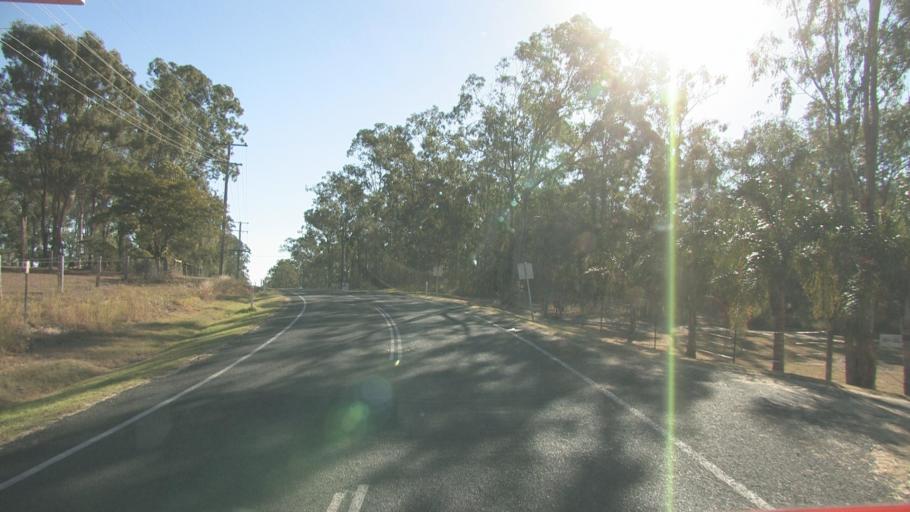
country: AU
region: Queensland
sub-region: Logan
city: North Maclean
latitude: -27.8040
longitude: 153.0337
